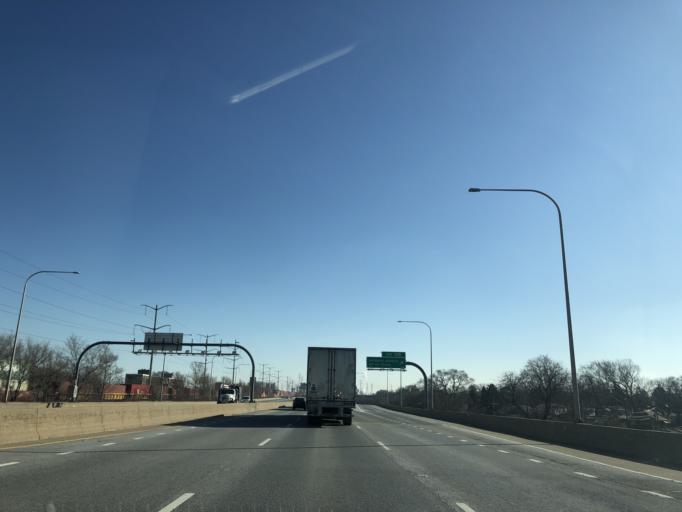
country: US
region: Indiana
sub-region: Lake County
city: Whiting
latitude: 41.7330
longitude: -87.5636
